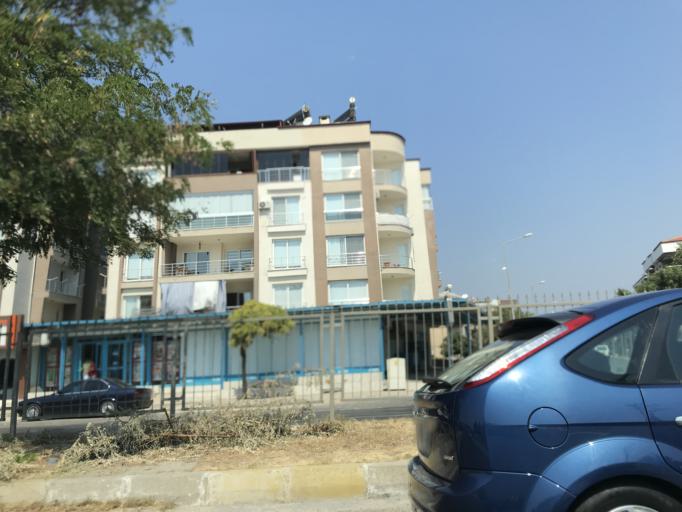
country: TR
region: Mugla
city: Milas
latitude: 37.3081
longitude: 27.7881
